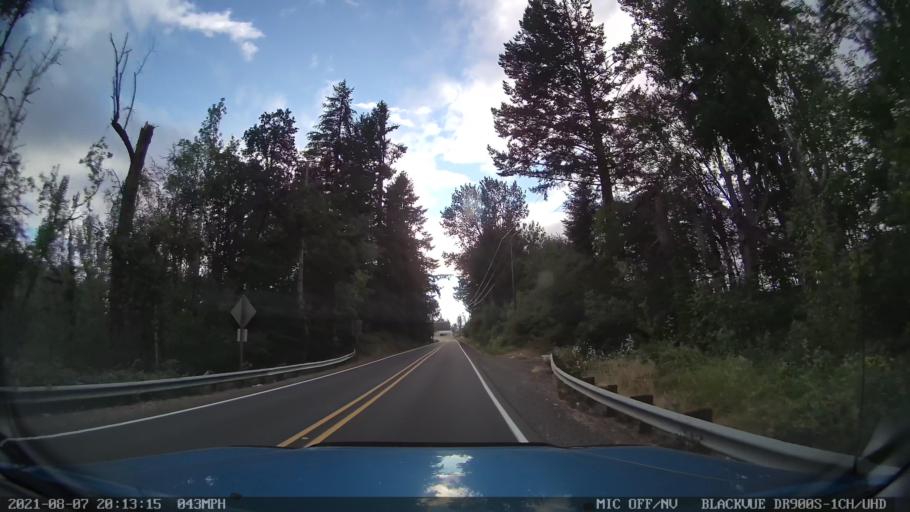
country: US
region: Oregon
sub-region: Marion County
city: Hayesville
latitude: 44.9565
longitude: -122.9210
